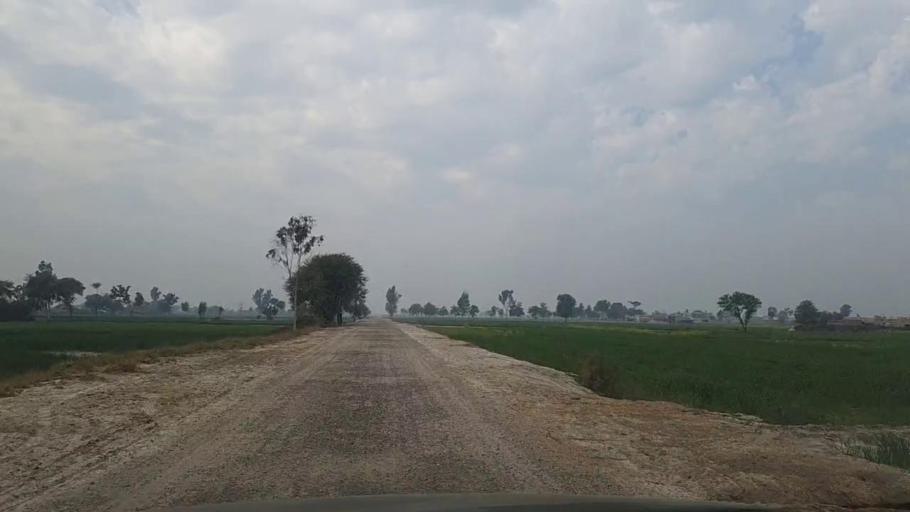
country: PK
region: Sindh
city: Nawabshah
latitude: 26.3560
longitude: 68.3961
